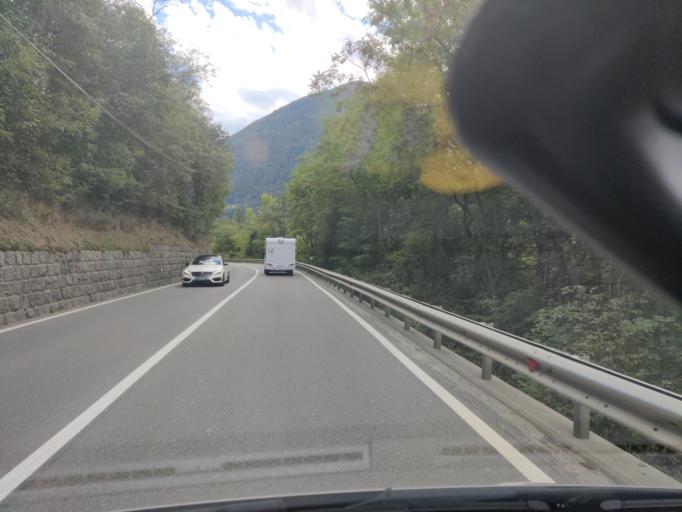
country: IT
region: Trentino-Alto Adige
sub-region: Bolzano
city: Varna
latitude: 46.7509
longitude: 11.6368
